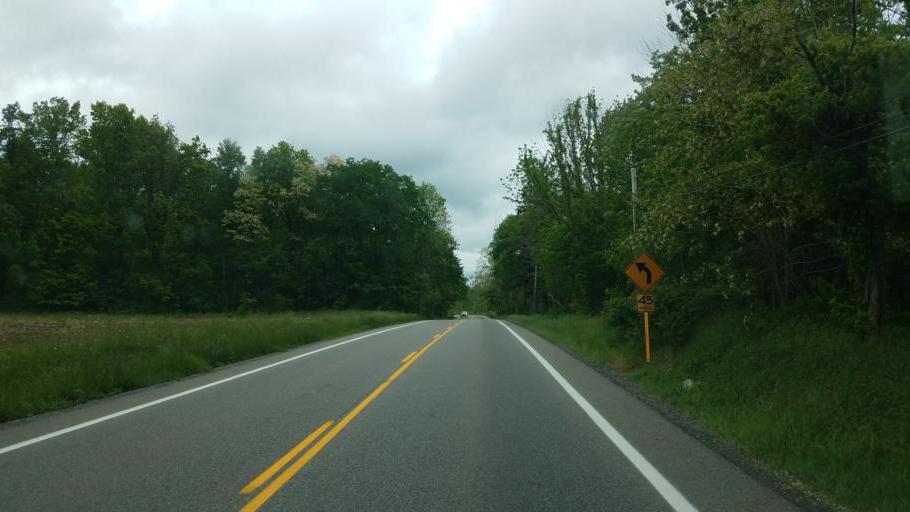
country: US
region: Ohio
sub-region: Portage County
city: Mantua
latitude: 41.3737
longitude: -81.2195
